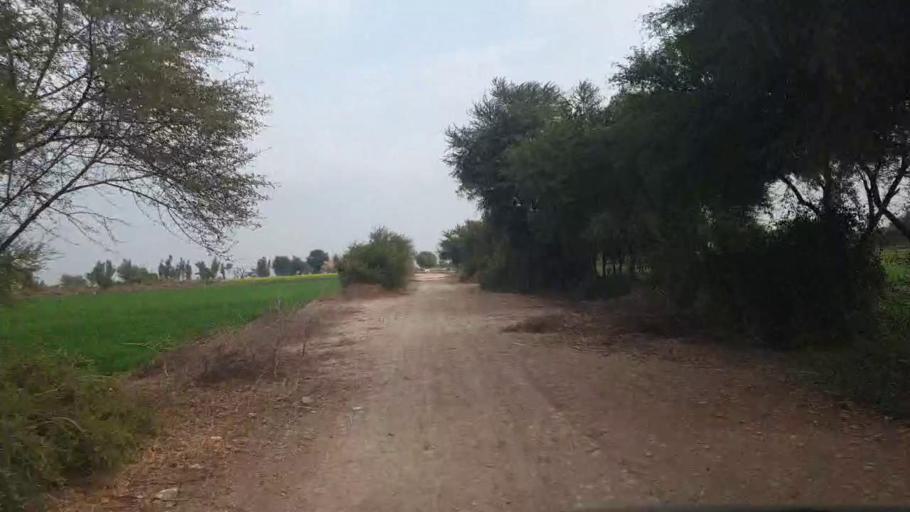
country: PK
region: Sindh
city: Shahdadpur
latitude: 25.8907
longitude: 68.6996
